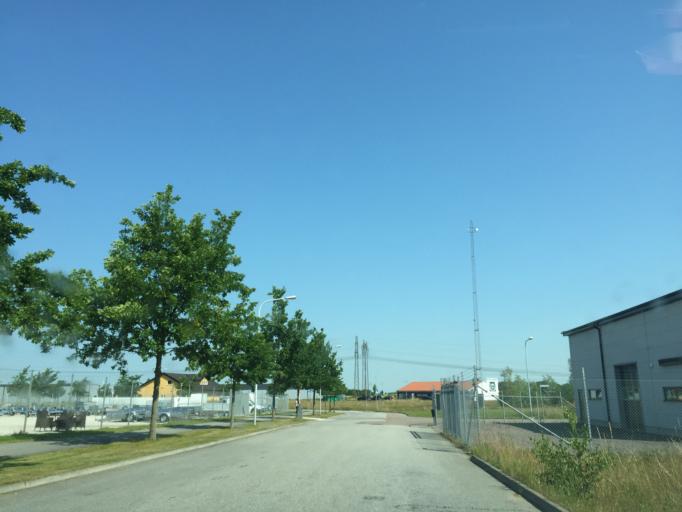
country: SE
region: Skane
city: Bjarred
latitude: 55.7384
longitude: 13.0350
